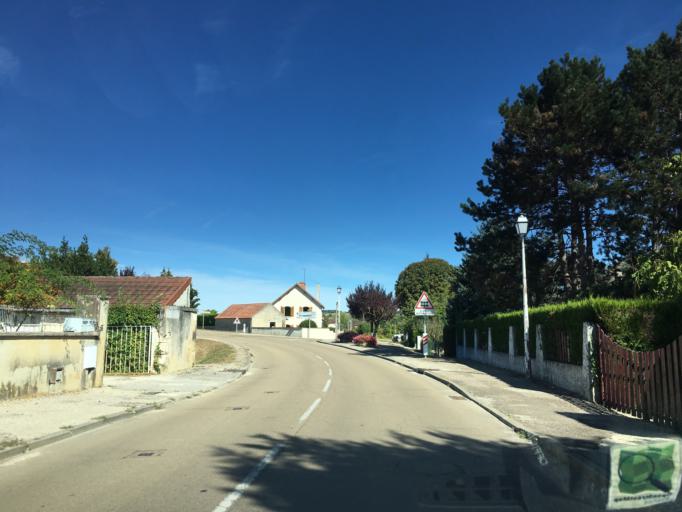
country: FR
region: Bourgogne
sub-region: Departement de l'Yonne
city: Vermenton
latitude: 47.6074
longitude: 3.6788
